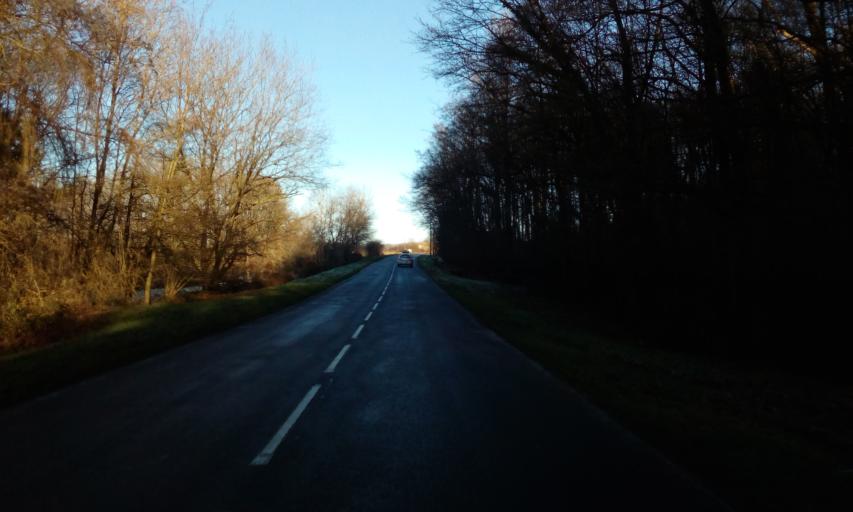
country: FR
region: Picardie
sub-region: Departement de l'Aisne
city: Rozoy-sur-Serre
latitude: 49.7286
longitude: 4.2743
